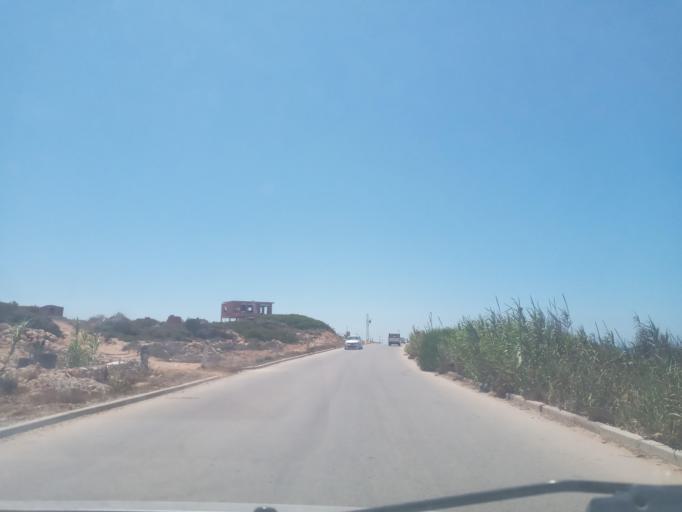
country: TN
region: Nabul
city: El Haouaria
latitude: 37.0514
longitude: 10.9861
